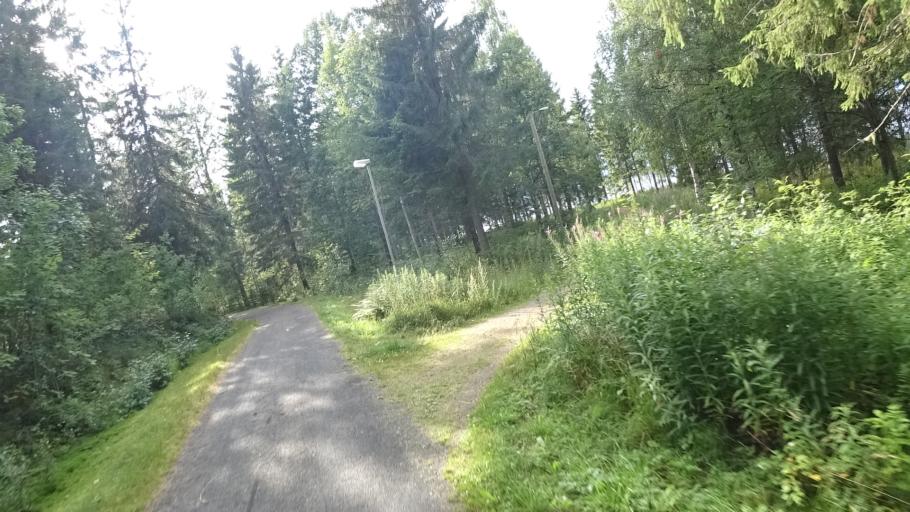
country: FI
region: North Karelia
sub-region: Joensuu
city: Ilomantsi
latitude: 62.6713
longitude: 30.9119
